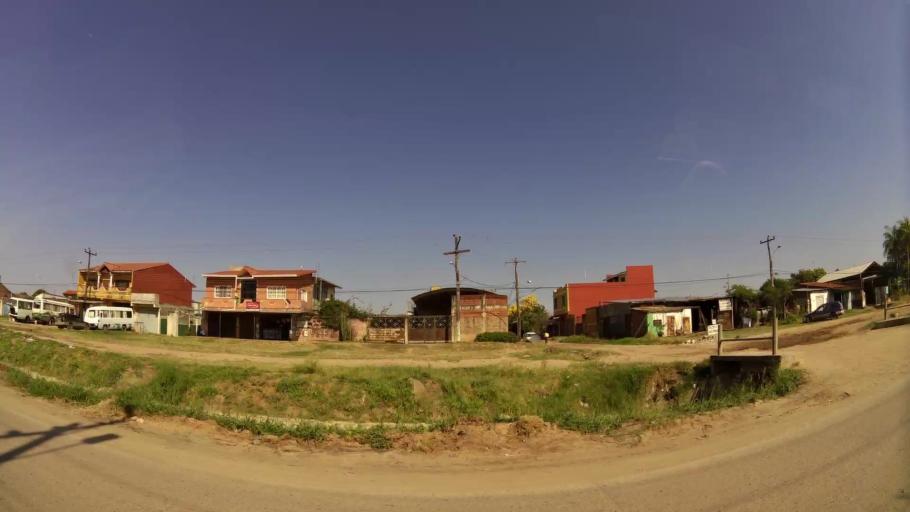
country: BO
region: Santa Cruz
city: Santa Cruz de la Sierra
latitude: -17.8226
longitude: -63.1266
